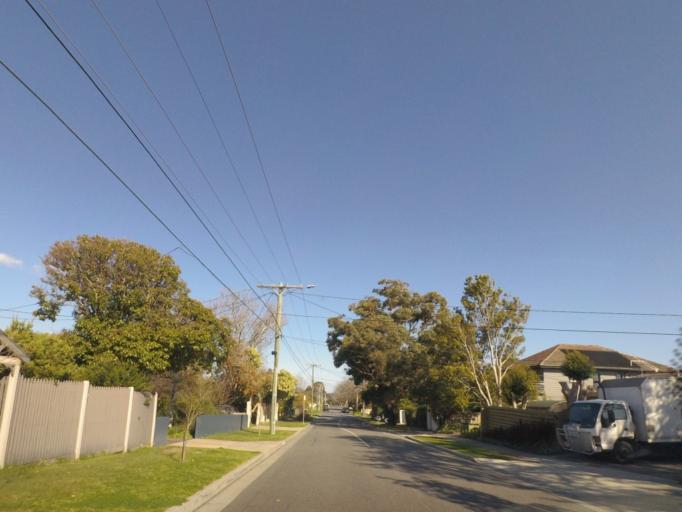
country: AU
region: Victoria
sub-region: Maroondah
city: Ringwood East
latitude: -37.8176
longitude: 145.2342
